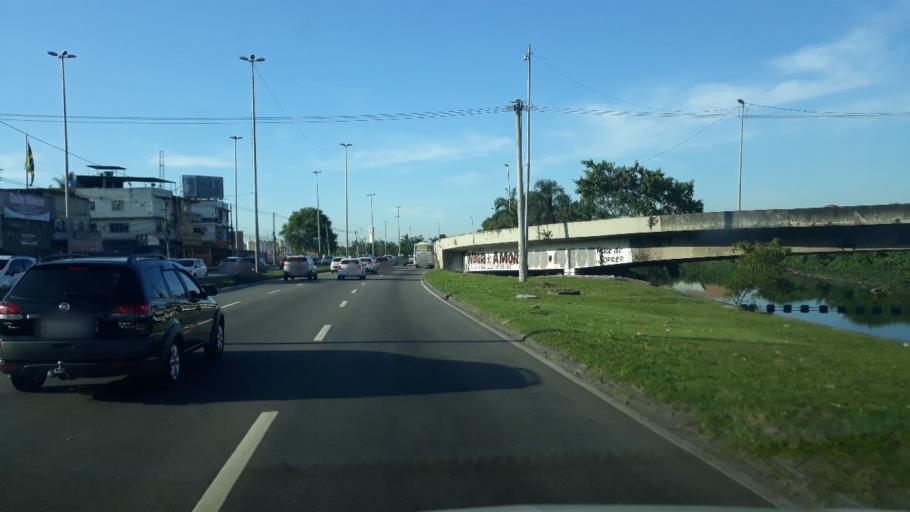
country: BR
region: Rio de Janeiro
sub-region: Sao Joao De Meriti
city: Sao Joao de Meriti
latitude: -22.9571
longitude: -43.3568
